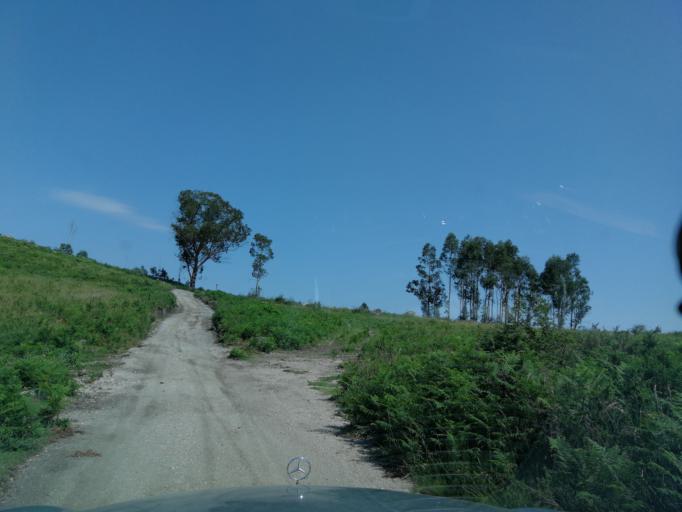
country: PT
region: Braga
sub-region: Povoa de Lanhoso
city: Povoa de Lanhoso
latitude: 41.5649
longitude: -8.3410
